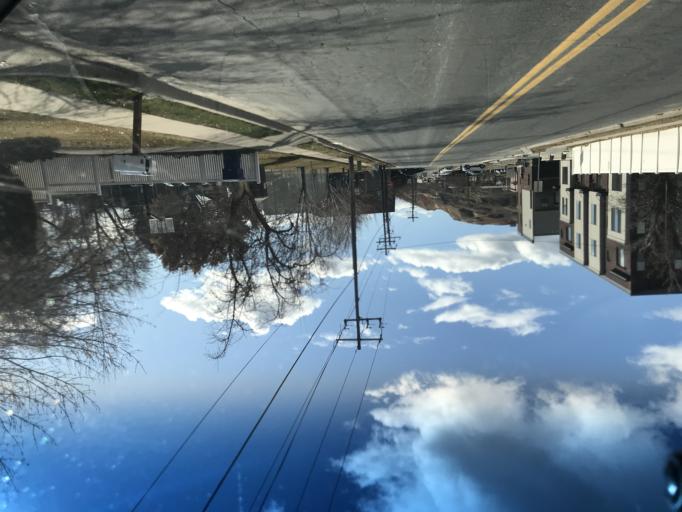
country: US
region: Utah
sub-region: Davis County
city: North Salt Lake
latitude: 40.8429
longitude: -111.9118
